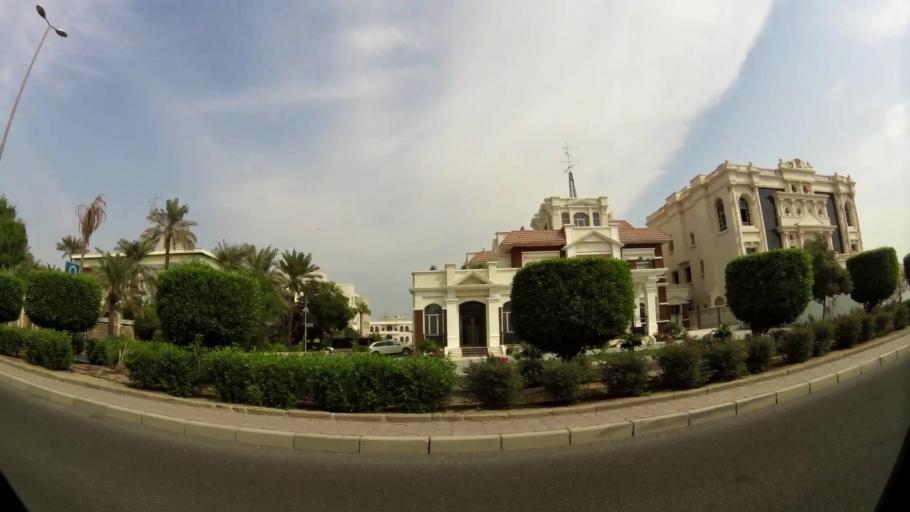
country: KW
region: Al Asimah
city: Kuwait City
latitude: 29.3523
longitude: 47.9856
